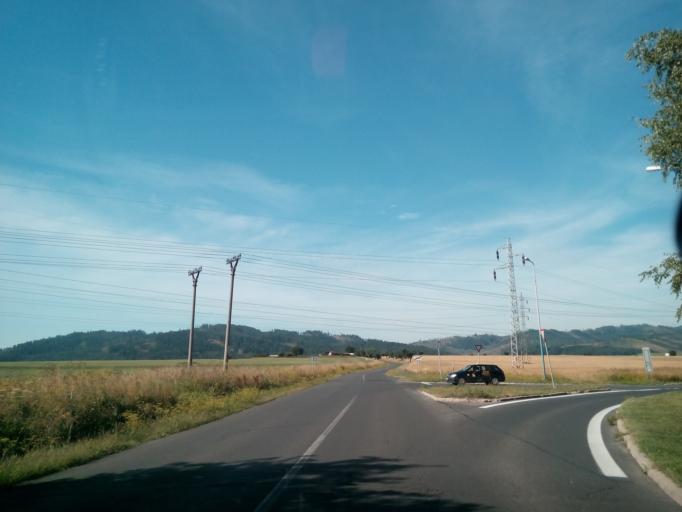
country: SK
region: Presovsky
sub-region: Okres Poprad
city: Poprad
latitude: 49.0425
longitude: 20.2864
